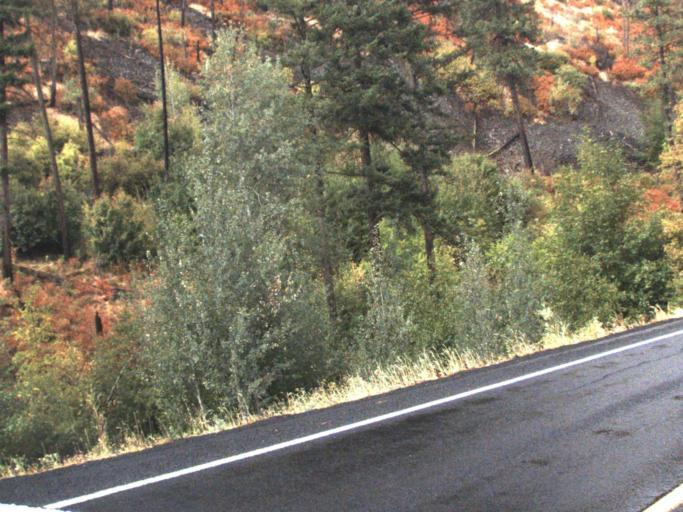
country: US
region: Washington
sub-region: Spokane County
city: Medical Lake
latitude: 47.7452
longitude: -117.8866
